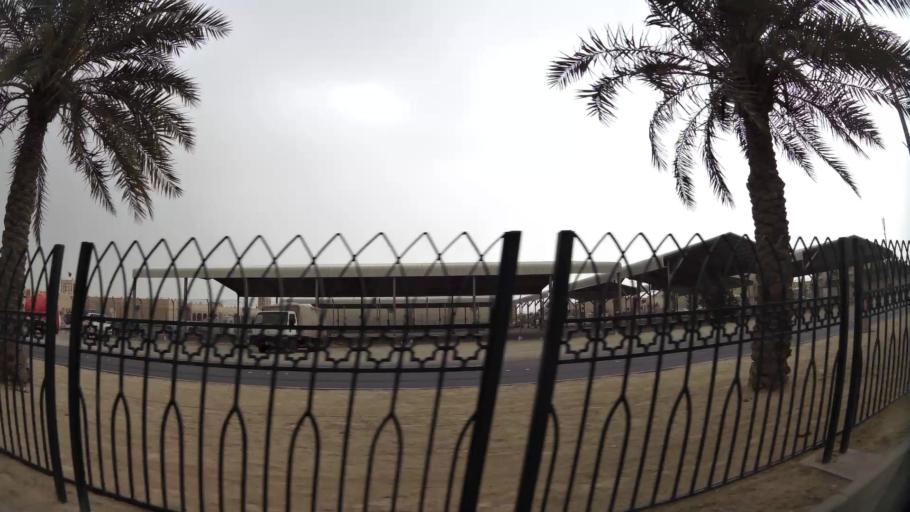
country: BH
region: Northern
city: Madinat `Isa
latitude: 26.1683
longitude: 50.5553
